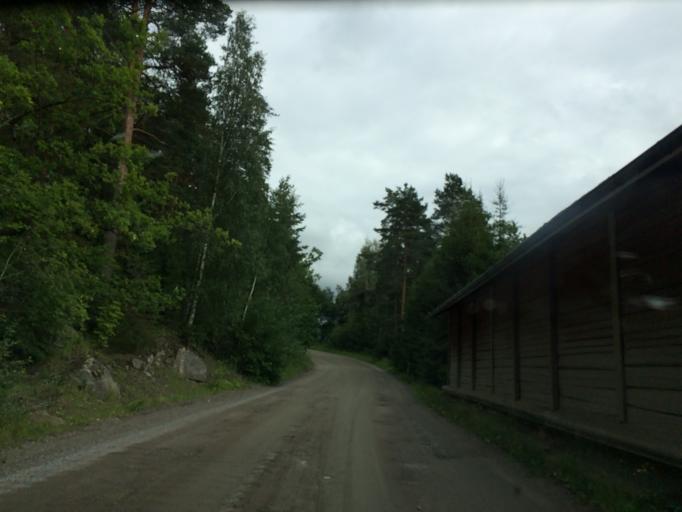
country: FI
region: Haeme
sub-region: Haemeenlinna
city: Haemeenlinna
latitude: 60.9686
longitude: 24.5221
